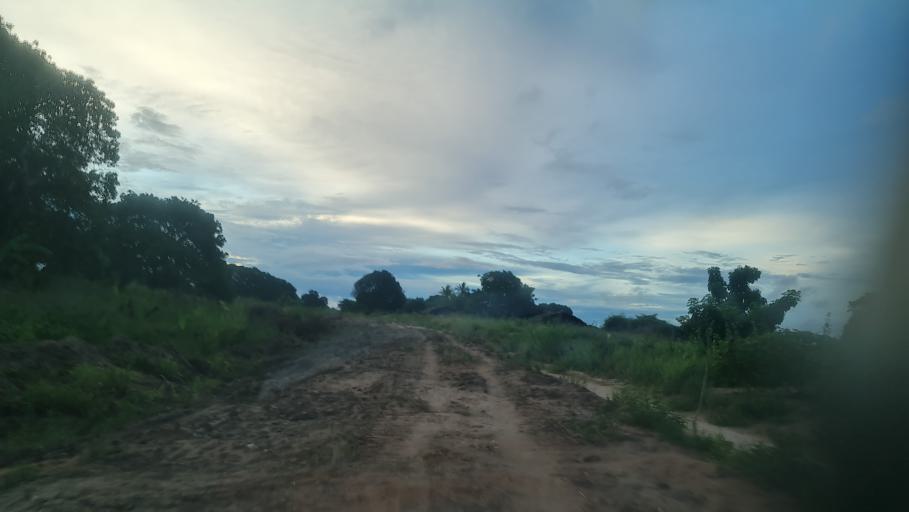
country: MZ
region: Nampula
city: Nampula
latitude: -14.7379
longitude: 39.9286
